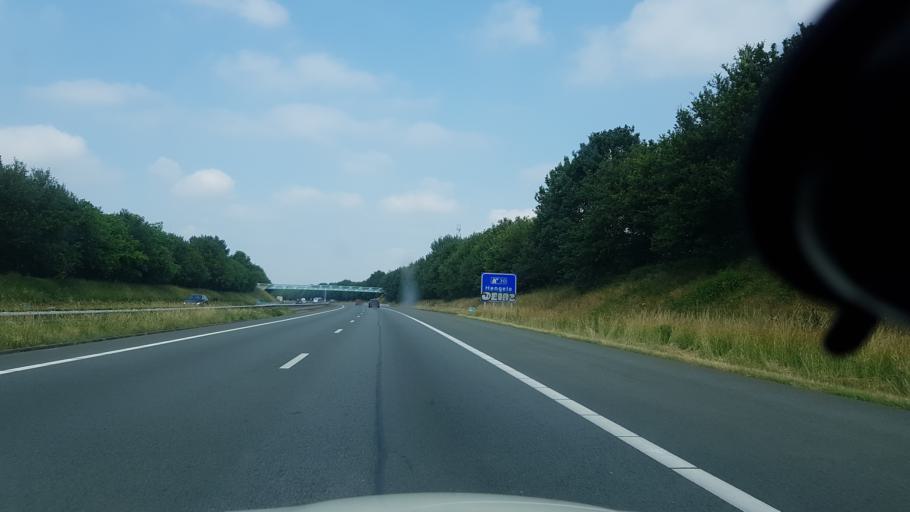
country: NL
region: Overijssel
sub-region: Gemeente Hengelo
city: Hengelo
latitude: 52.2856
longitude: 6.8014
